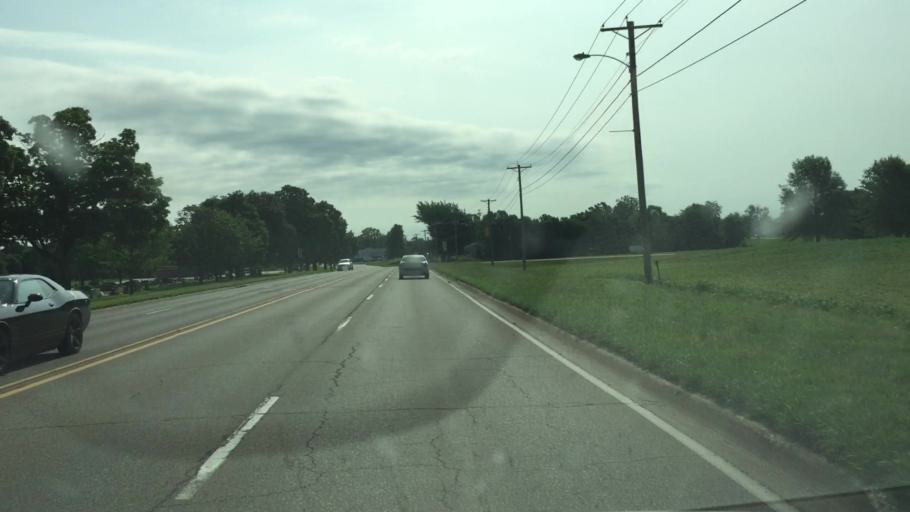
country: US
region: Iowa
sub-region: Lee County
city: Fort Madison
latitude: 40.6238
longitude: -91.3676
